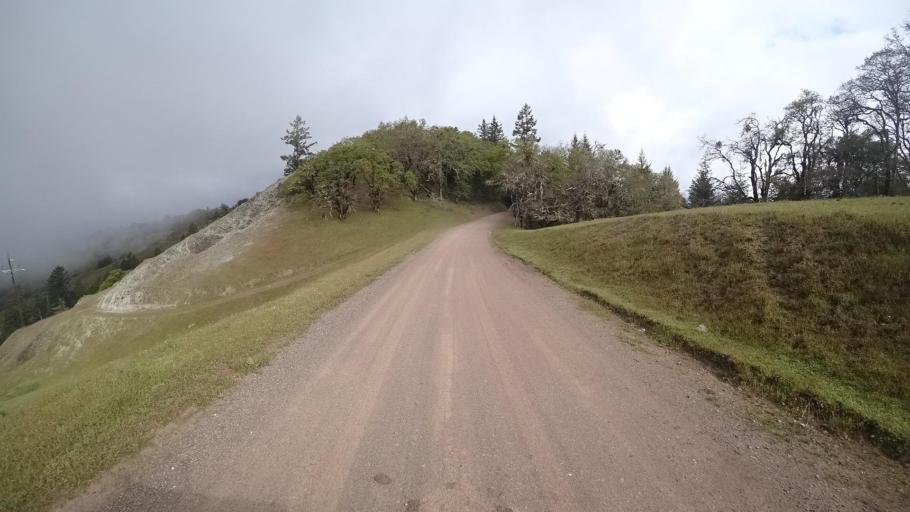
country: US
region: California
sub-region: Humboldt County
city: Redway
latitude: 40.2032
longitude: -123.7162
